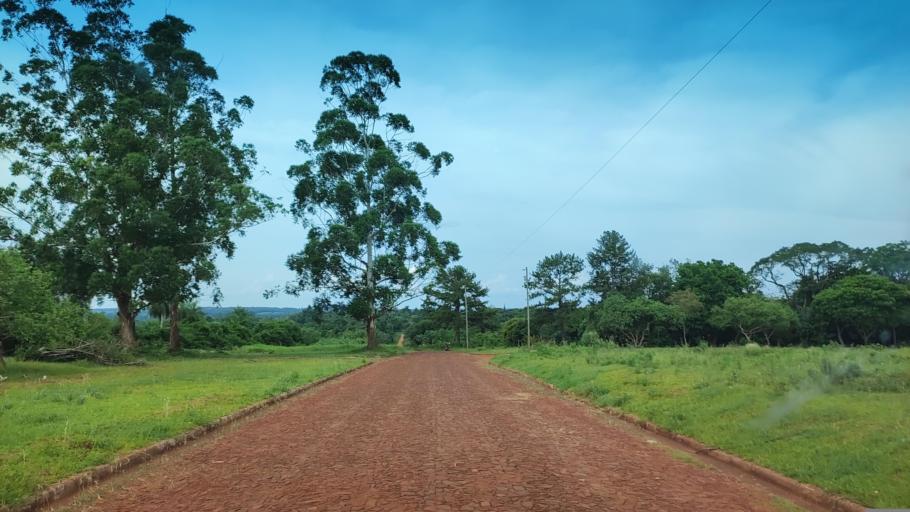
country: AR
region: Misiones
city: Gobernador Roca
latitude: -27.1269
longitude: -55.5149
